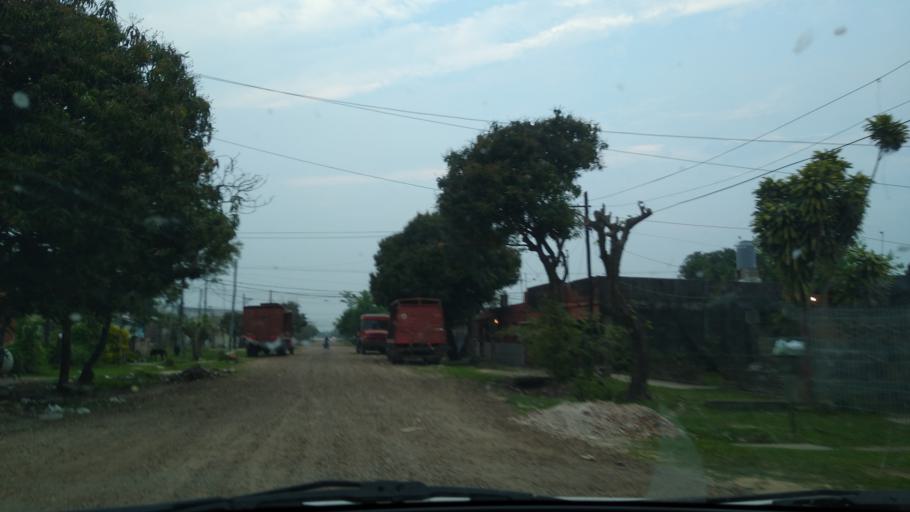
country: AR
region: Chaco
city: Barranqueras
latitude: -27.4891
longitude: -58.9534
